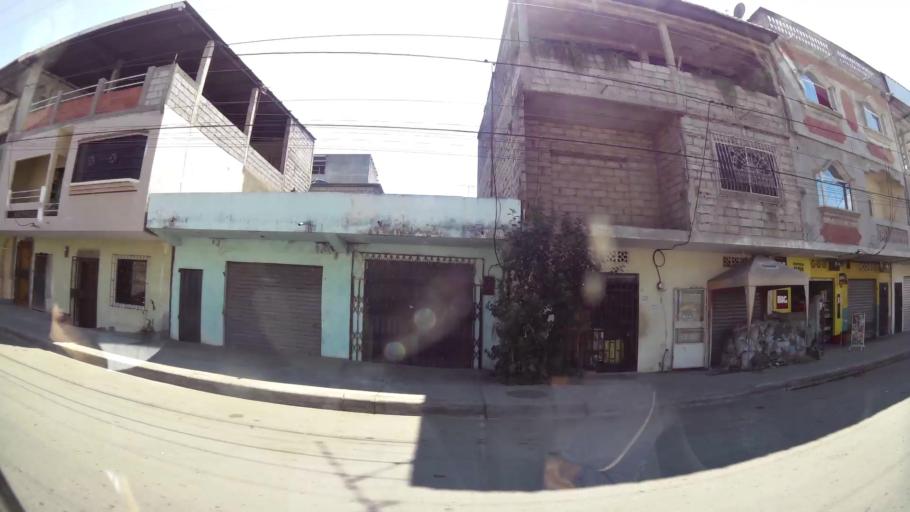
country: EC
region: Guayas
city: Guayaquil
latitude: -2.1911
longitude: -79.9452
